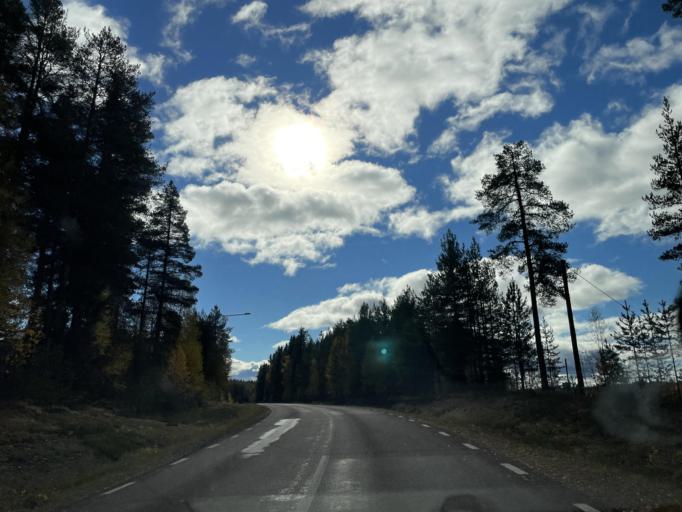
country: NO
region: Hedmark
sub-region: Trysil
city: Innbygda
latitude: 61.4913
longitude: 13.0816
